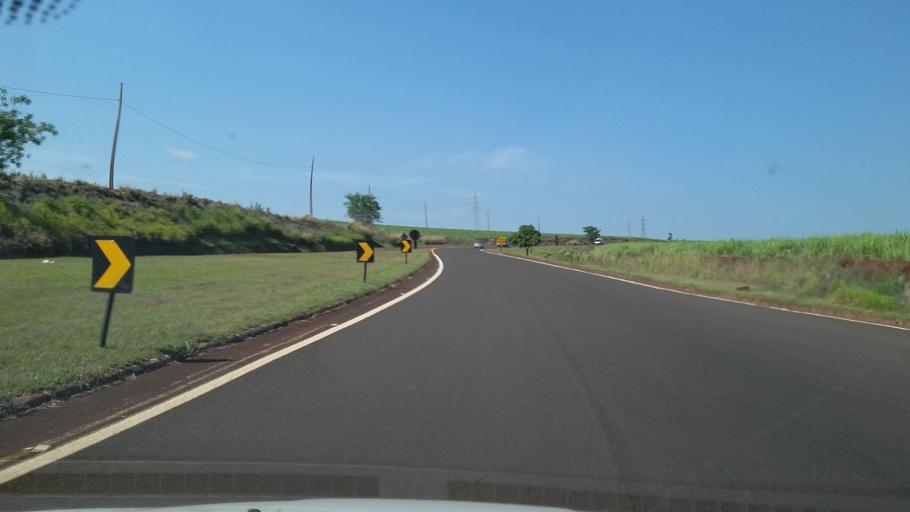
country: BR
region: Parana
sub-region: Bandeirantes
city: Bandeirantes
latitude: -23.1111
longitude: -50.3353
